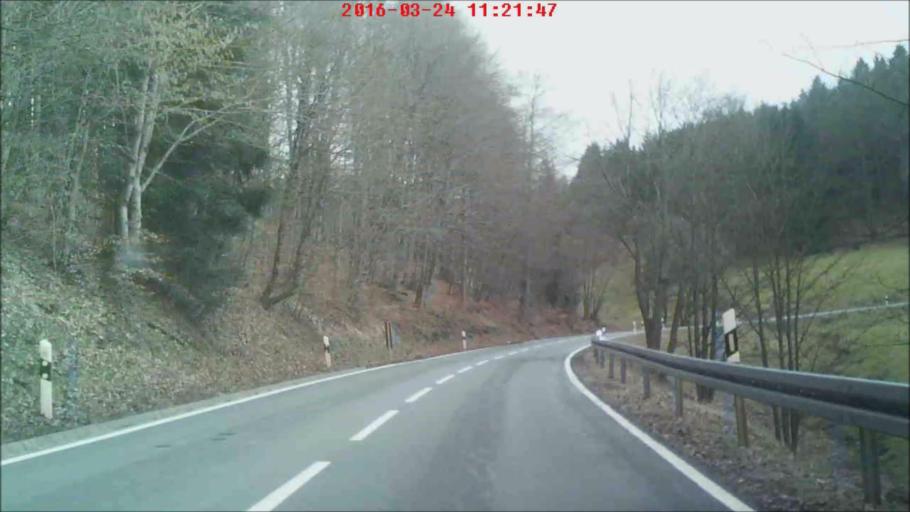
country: DE
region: Thuringia
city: Eisfeld
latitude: 50.4868
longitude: 10.9172
